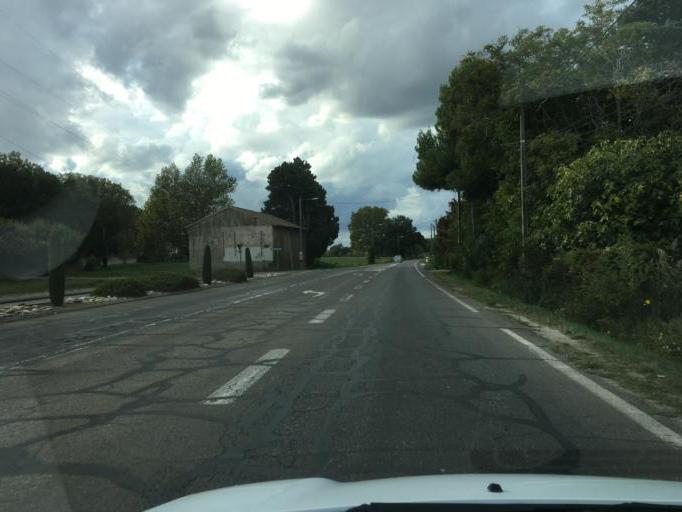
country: FR
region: Provence-Alpes-Cote d'Azur
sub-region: Departement du Vaucluse
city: Morieres-les-Avignon
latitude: 43.9419
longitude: 4.8906
